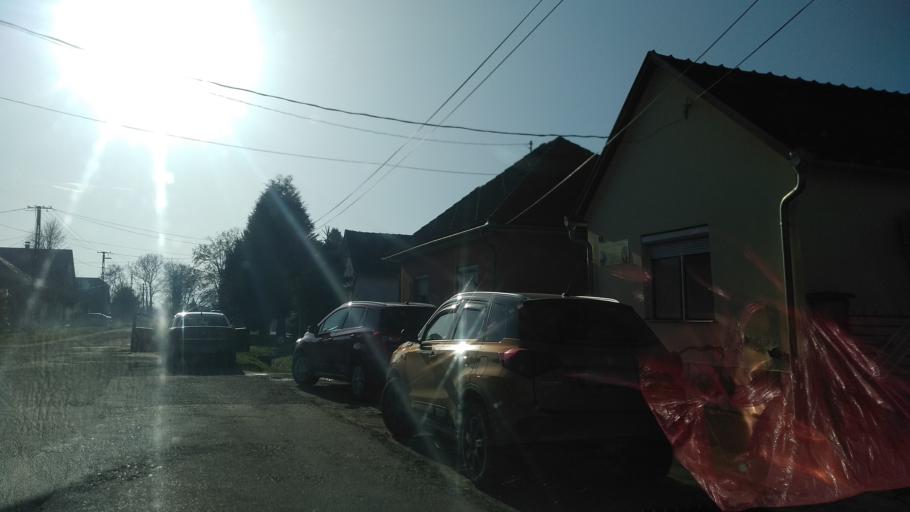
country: HU
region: Somogy
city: Barcs
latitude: 45.9605
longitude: 17.4820
